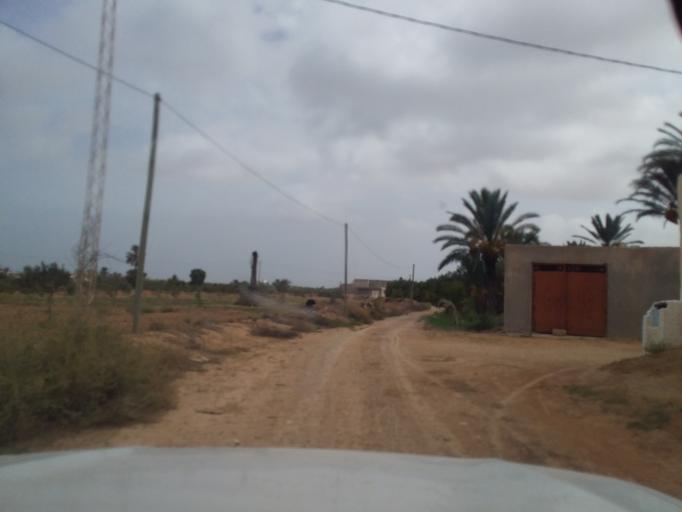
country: TN
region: Qabis
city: Gabes
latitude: 33.6282
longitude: 10.3078
